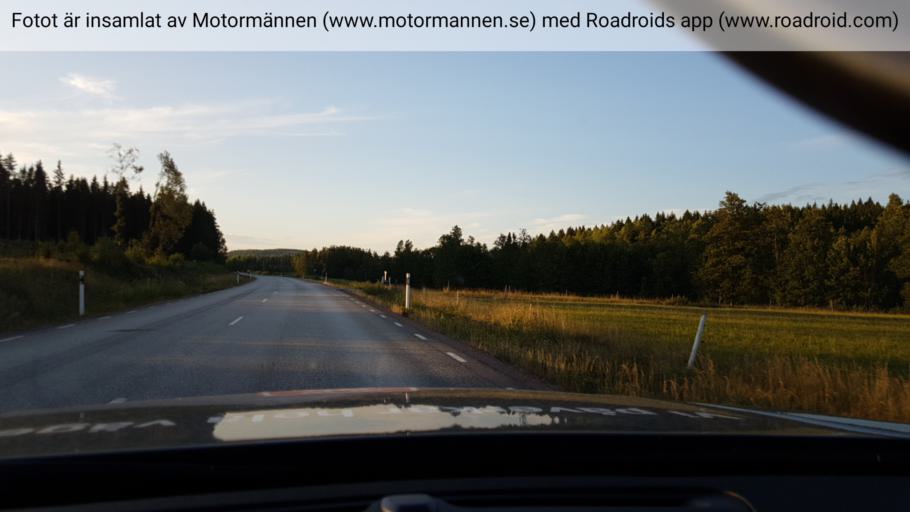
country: SE
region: Vaermland
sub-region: Storfors Kommun
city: Storfors
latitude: 59.4846
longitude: 14.3288
